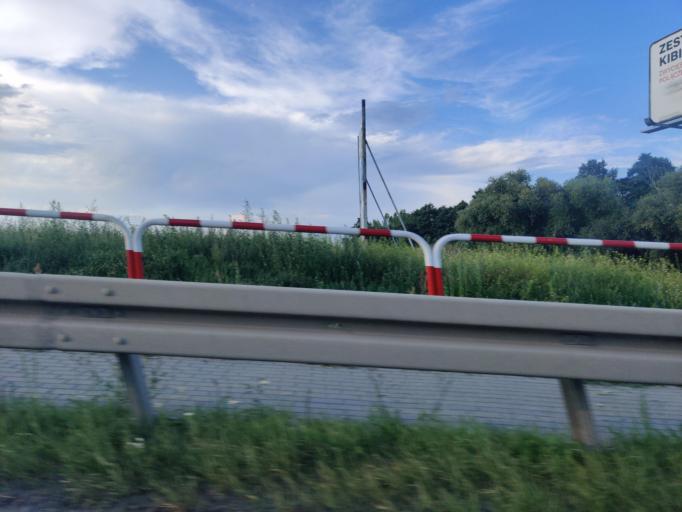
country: PL
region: Greater Poland Voivodeship
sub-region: Konin
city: Konin
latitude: 52.1988
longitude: 18.2931
